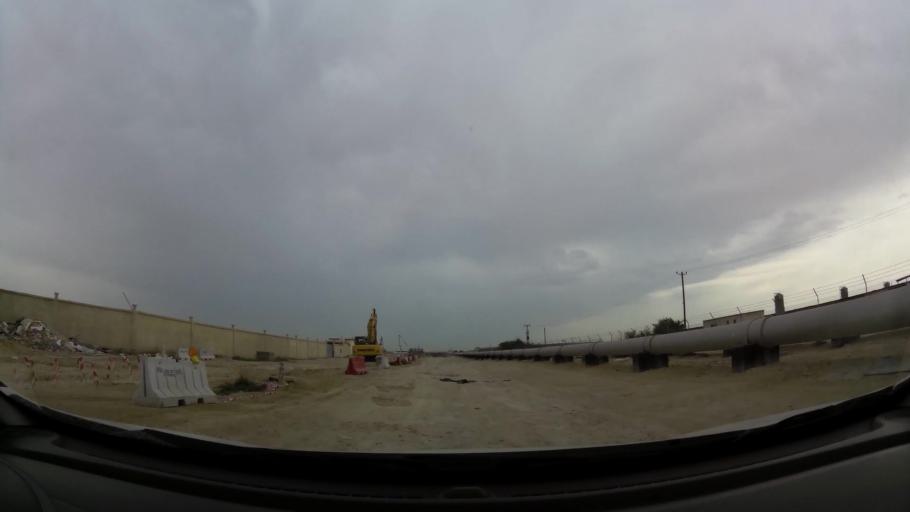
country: BH
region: Central Governorate
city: Madinat Hamad
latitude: 26.1437
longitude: 50.4798
